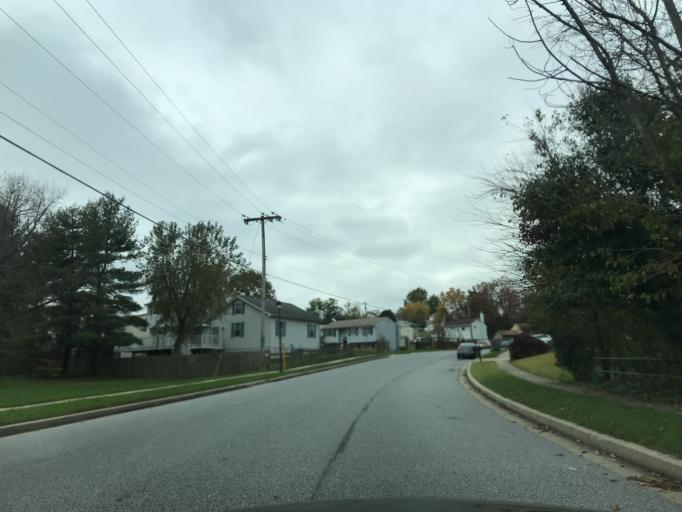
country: US
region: Maryland
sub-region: Baltimore County
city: Carney
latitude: 39.3860
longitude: -76.5153
